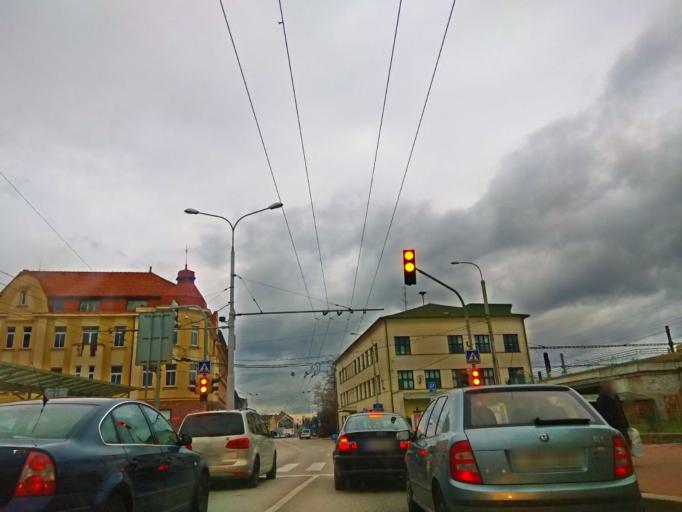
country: CZ
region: Jihocesky
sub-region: Okres Ceske Budejovice
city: Ceske Budejovice
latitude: 48.9747
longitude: 14.4876
